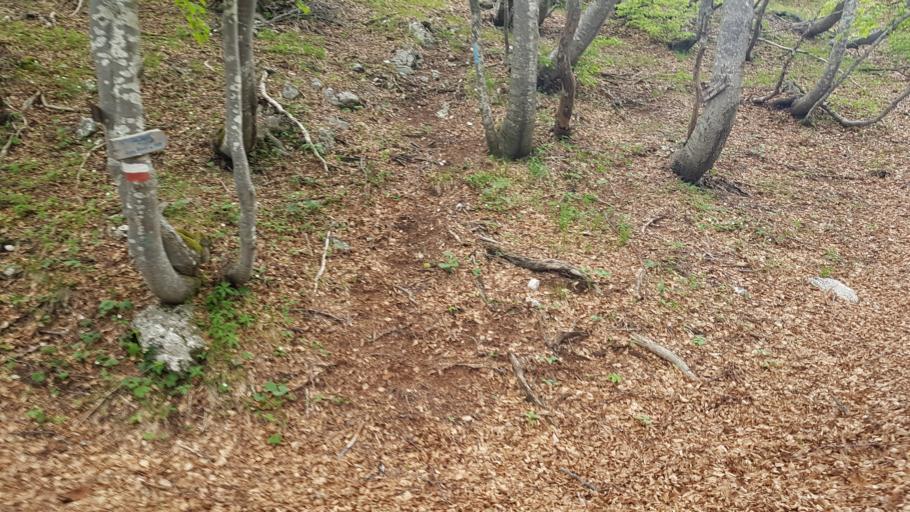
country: IT
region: Friuli Venezia Giulia
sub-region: Provincia di Udine
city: Moggio Udinese
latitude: 46.4781
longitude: 13.2092
